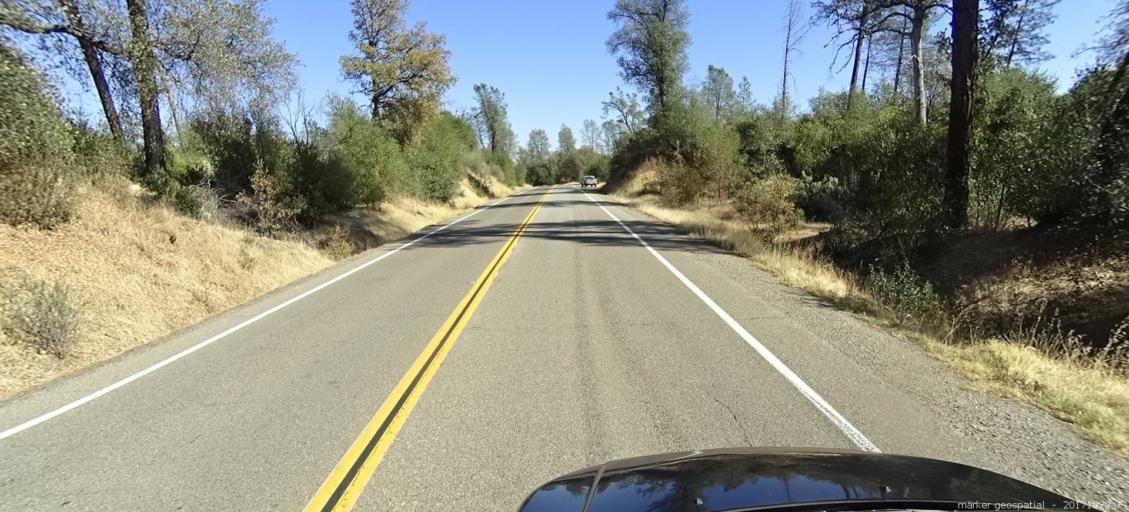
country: US
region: California
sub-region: Shasta County
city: Shasta
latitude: 40.4944
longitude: -122.4662
